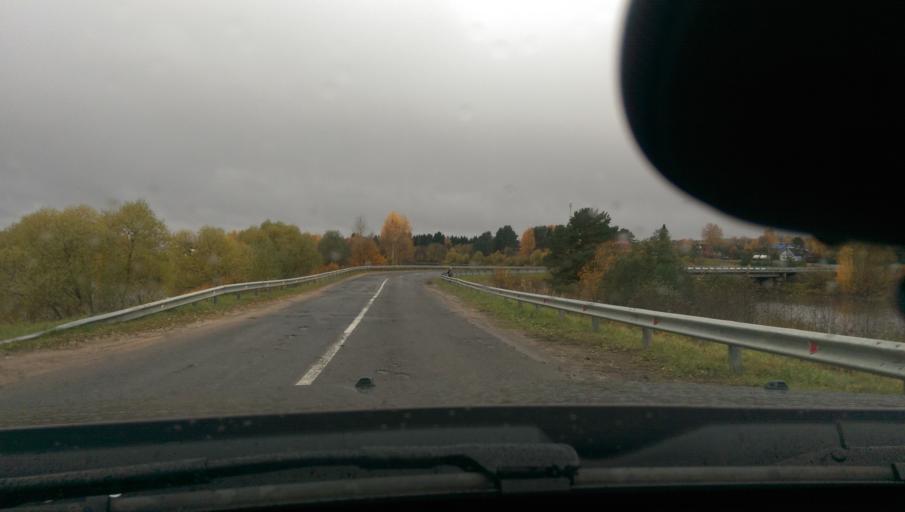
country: RU
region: Jaroslavl
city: Poshekhon'ye
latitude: 58.5164
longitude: 39.1249
